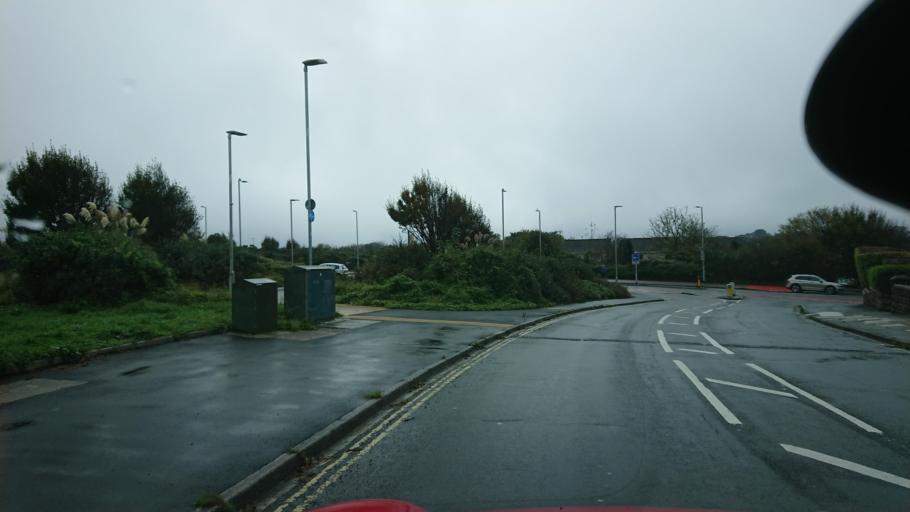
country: GB
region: England
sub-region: Plymouth
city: Plymouth
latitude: 50.4279
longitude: -4.1144
